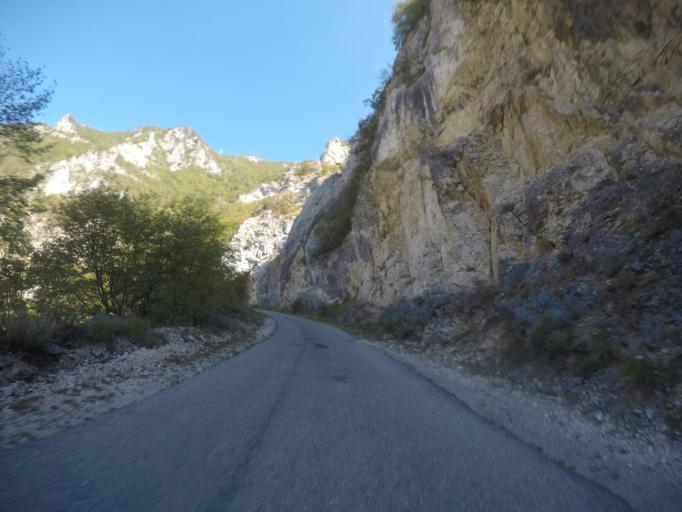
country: ME
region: Opstina Pluzine
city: Pluzine
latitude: 43.1699
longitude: 18.8596
